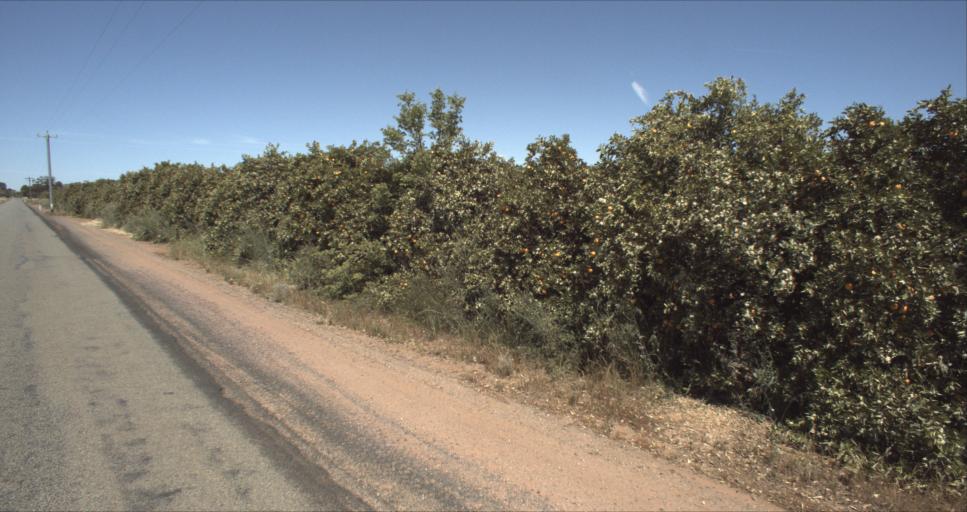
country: AU
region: New South Wales
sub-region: Leeton
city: Leeton
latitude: -34.5402
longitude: 146.3621
